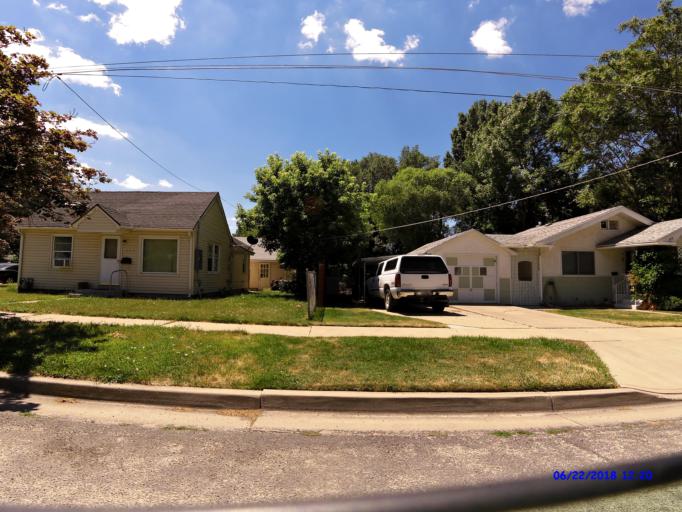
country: US
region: Utah
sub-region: Weber County
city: Ogden
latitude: 41.2397
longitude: -111.9676
